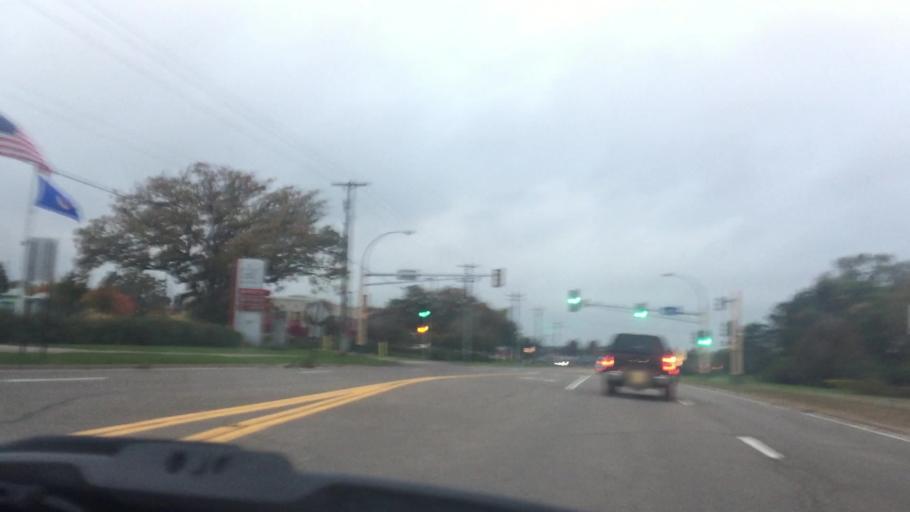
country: US
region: Minnesota
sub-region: Anoka County
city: Spring Lake Park
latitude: 45.1080
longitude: -93.2563
